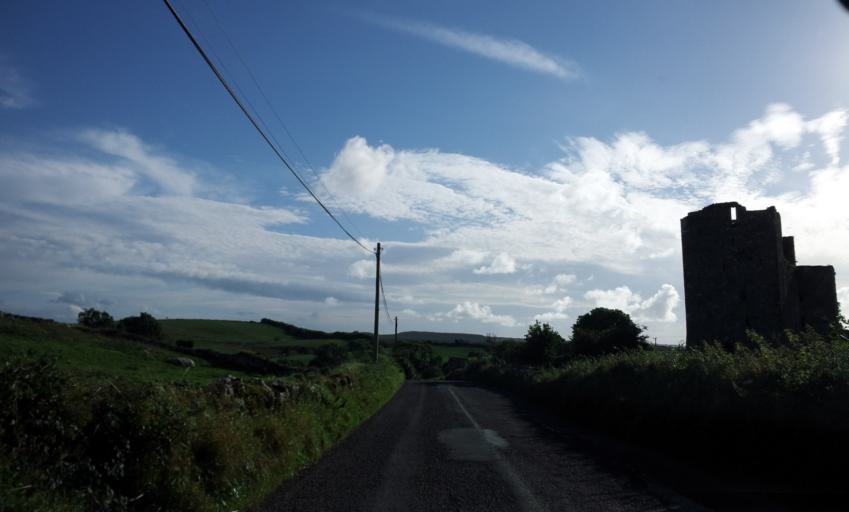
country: IE
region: Munster
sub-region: An Clar
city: Ennis
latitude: 52.9884
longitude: -9.1380
